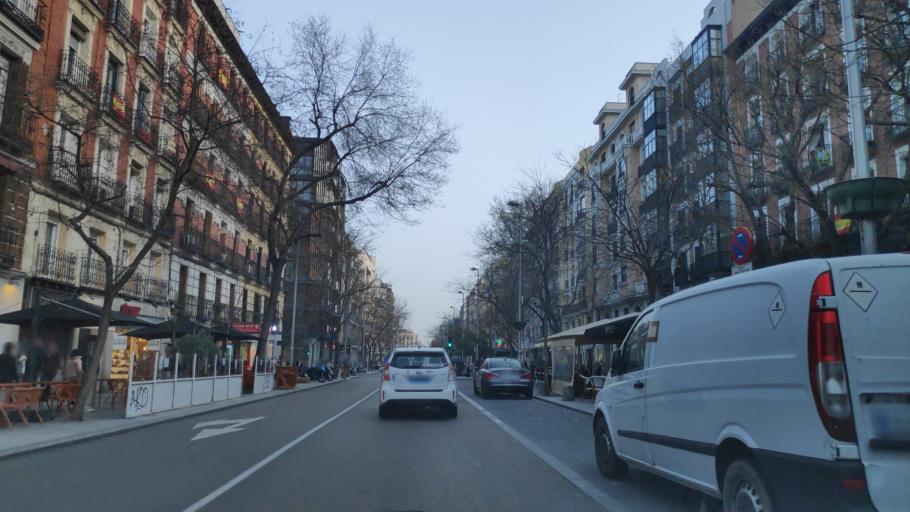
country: ES
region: Madrid
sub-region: Provincia de Madrid
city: Chamberi
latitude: 40.4327
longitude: -3.7040
